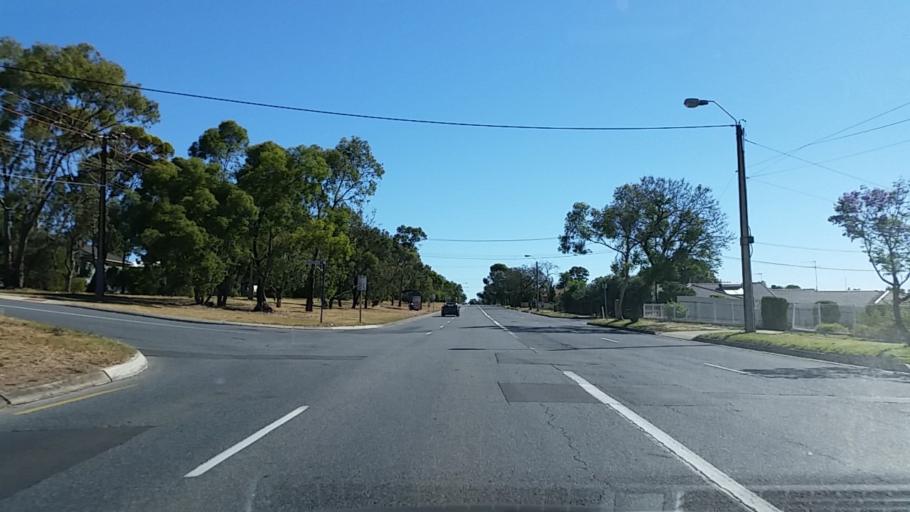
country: AU
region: South Australia
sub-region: Salisbury
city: Ingle Farm
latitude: -34.8297
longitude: 138.6309
